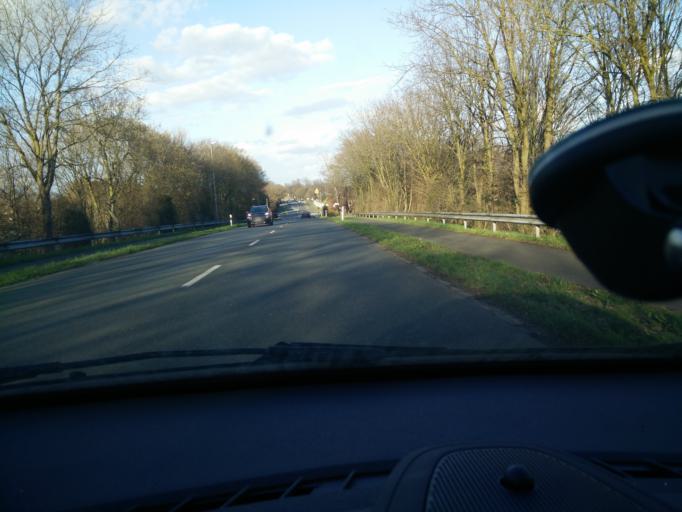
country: DE
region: North Rhine-Westphalia
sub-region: Regierungsbezirk Dusseldorf
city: Wesel
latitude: 51.6727
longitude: 6.6226
